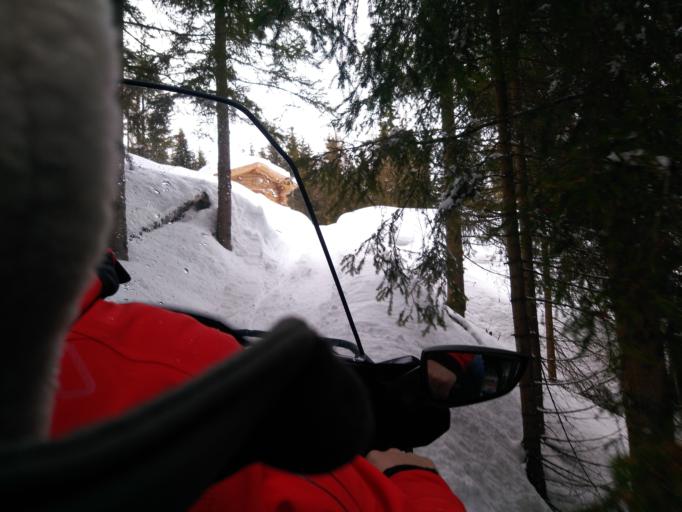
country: IT
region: Veneto
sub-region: Provincia di Belluno
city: Rocca Pietore
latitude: 46.4184
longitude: 11.9816
